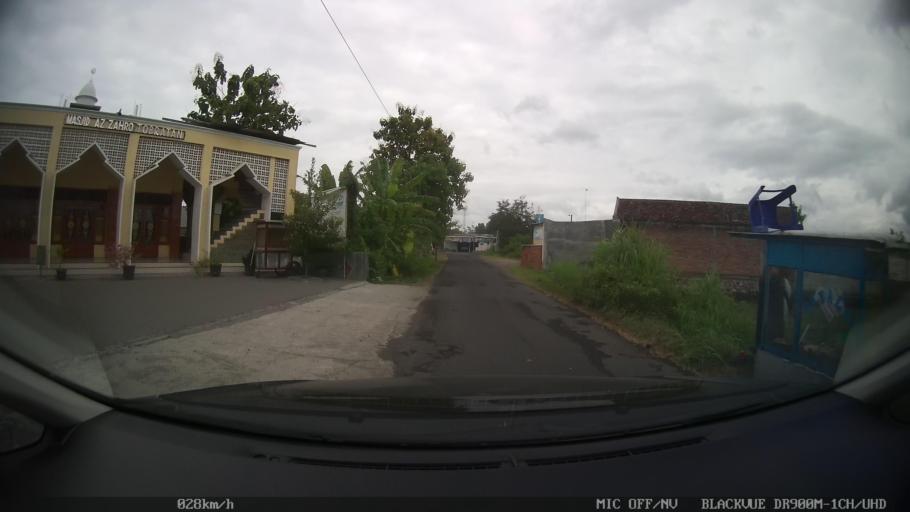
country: ID
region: Daerah Istimewa Yogyakarta
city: Sewon
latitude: -7.8615
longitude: 110.4014
